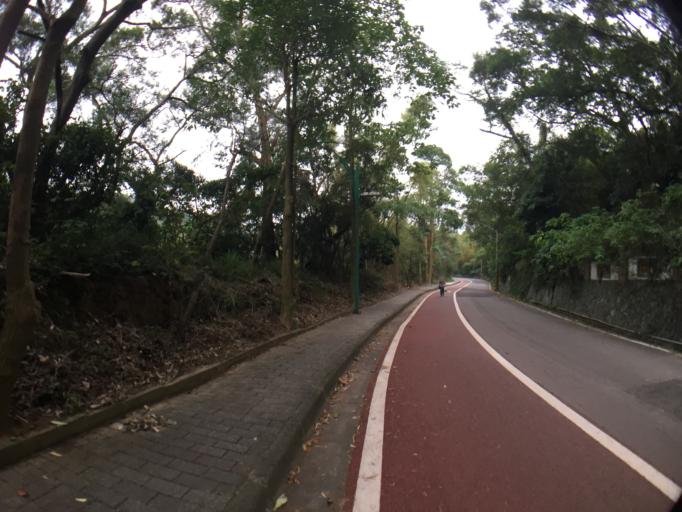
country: TW
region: Taiwan
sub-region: Hsinchu
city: Hsinchu
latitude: 24.7730
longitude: 120.9733
